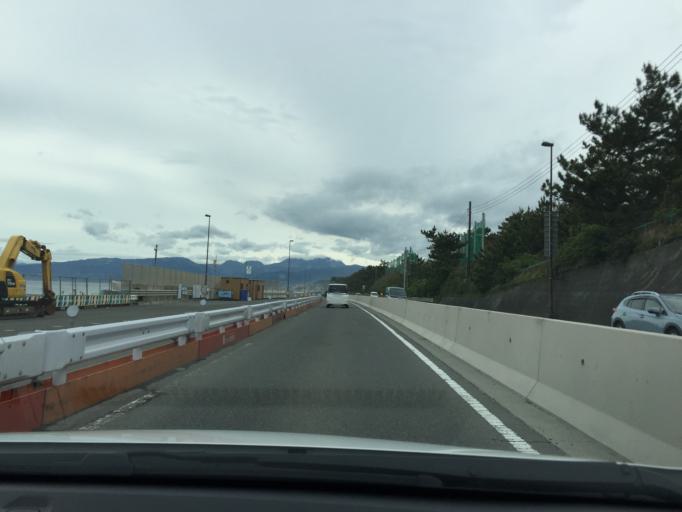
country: JP
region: Kanagawa
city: Ninomiya
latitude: 35.2988
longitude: 139.2735
